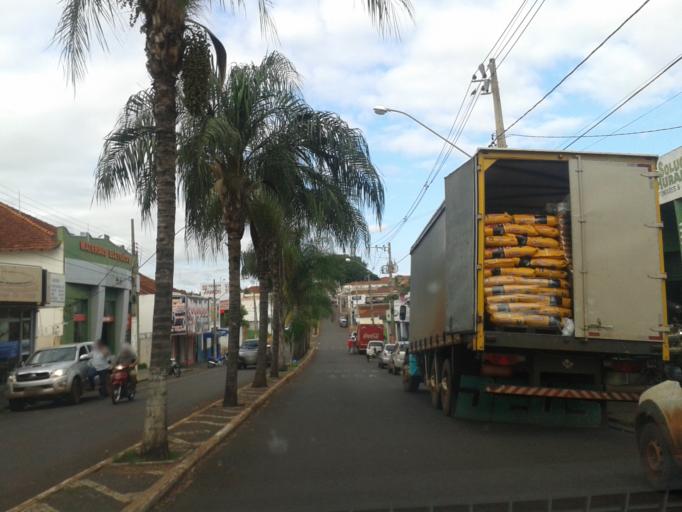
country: BR
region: Minas Gerais
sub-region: Ituiutaba
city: Ituiutaba
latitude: -18.9762
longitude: -49.4685
